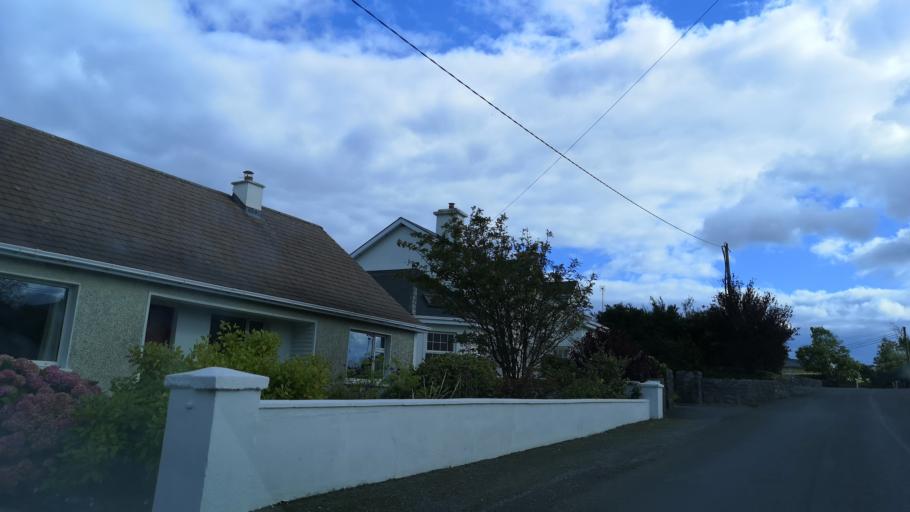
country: IE
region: Connaught
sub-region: County Galway
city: Moycullen
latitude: 53.3497
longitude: -9.1730
